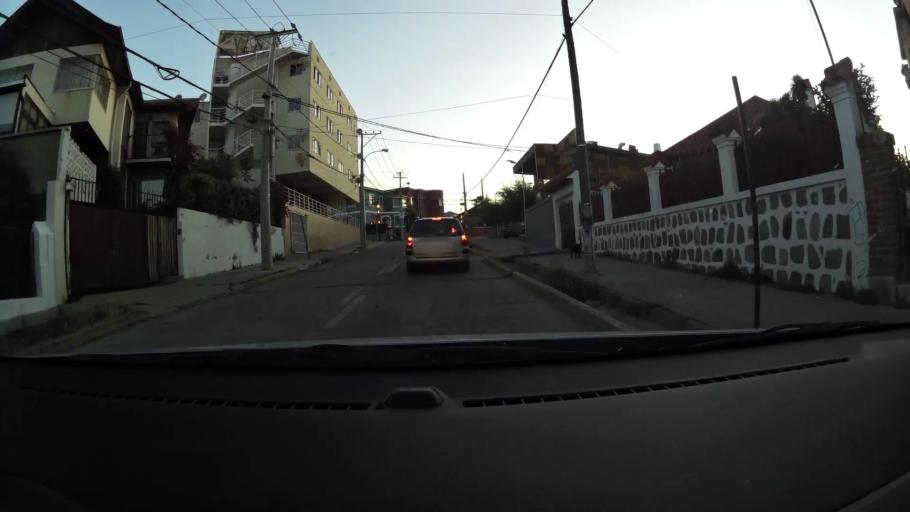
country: CL
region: Valparaiso
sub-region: Provincia de Valparaiso
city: Vina del Mar
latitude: -33.0262
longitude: -71.5711
